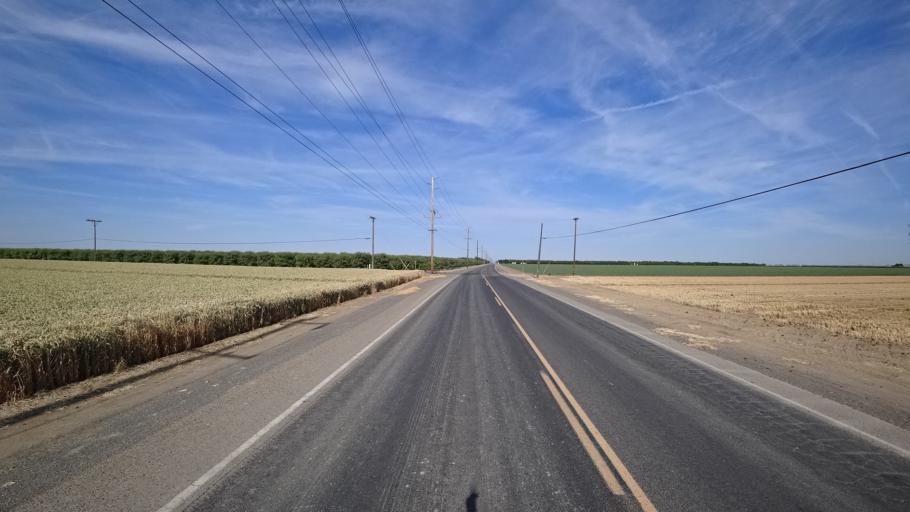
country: US
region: California
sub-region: Tulare County
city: Goshen
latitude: 36.3418
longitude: -119.4748
